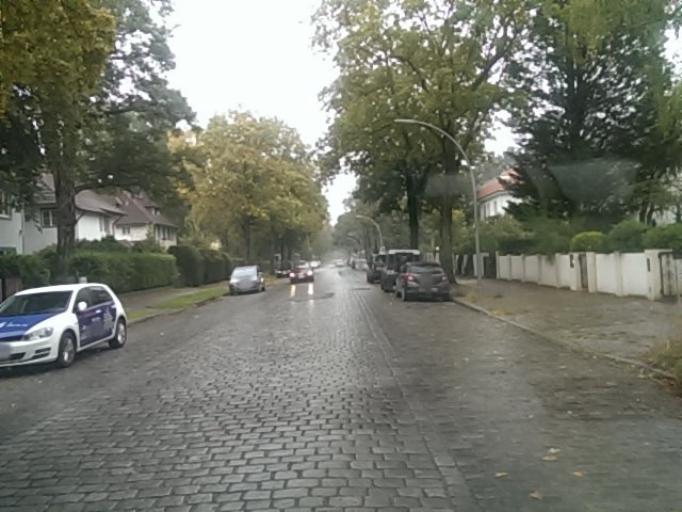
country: DE
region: Berlin
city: Lichterfelde
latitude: 52.4313
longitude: 13.2879
